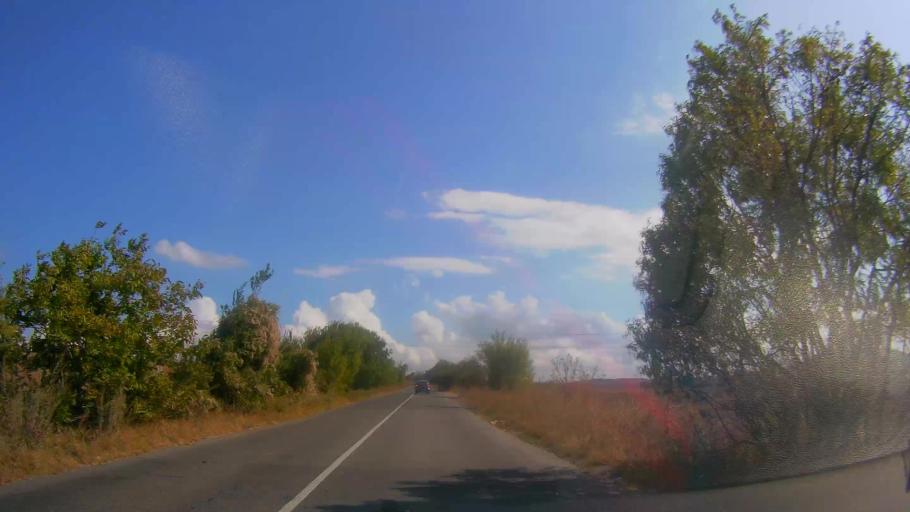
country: BG
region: Burgas
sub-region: Obshtina Burgas
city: Burgas
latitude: 42.4795
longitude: 27.3883
